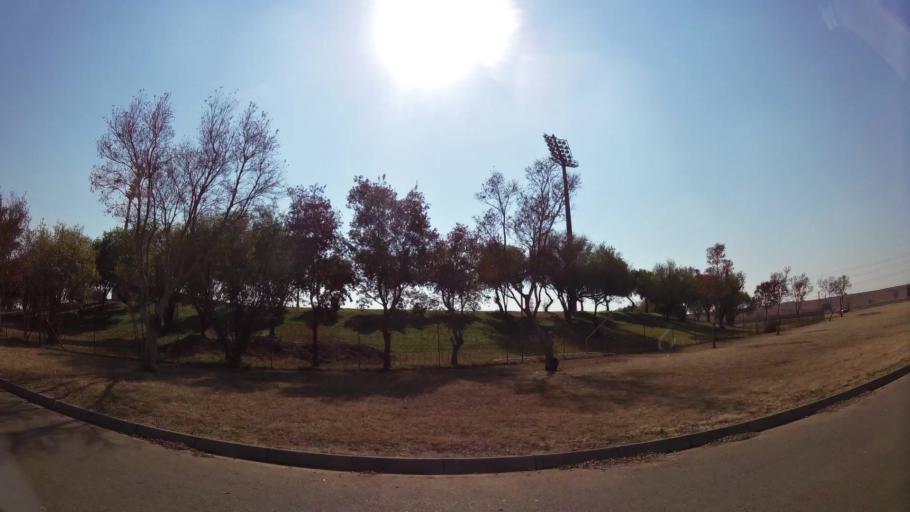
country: ZA
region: Gauteng
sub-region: Ekurhuleni Metropolitan Municipality
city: Boksburg
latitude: -26.2373
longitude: 28.2791
